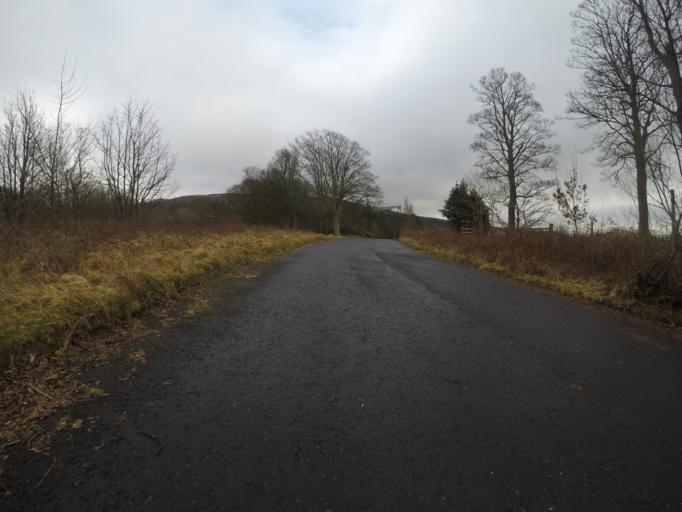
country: GB
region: Scotland
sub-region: North Ayrshire
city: Fairlie
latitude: 55.7292
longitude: -4.8690
